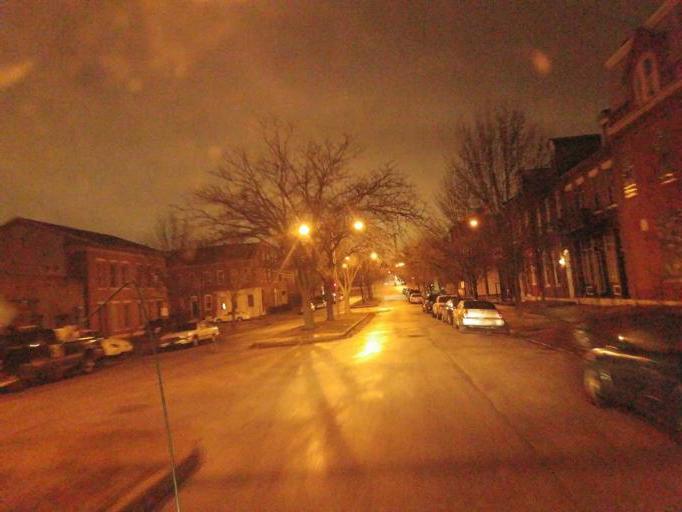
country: US
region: Missouri
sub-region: City of Saint Louis
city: St. Louis
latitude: 38.6480
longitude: -90.1966
